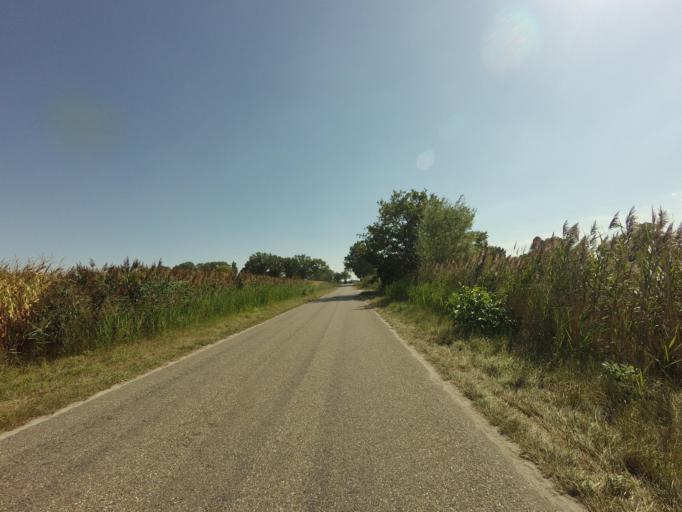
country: NL
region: North Brabant
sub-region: Gemeente Someren
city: Someren
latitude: 51.3788
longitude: 5.6729
